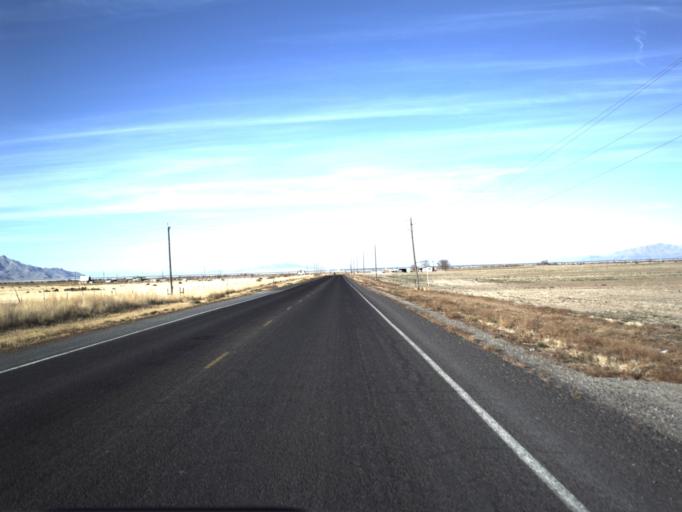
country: US
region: Utah
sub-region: Tooele County
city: Erda
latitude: 40.6034
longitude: -112.3707
